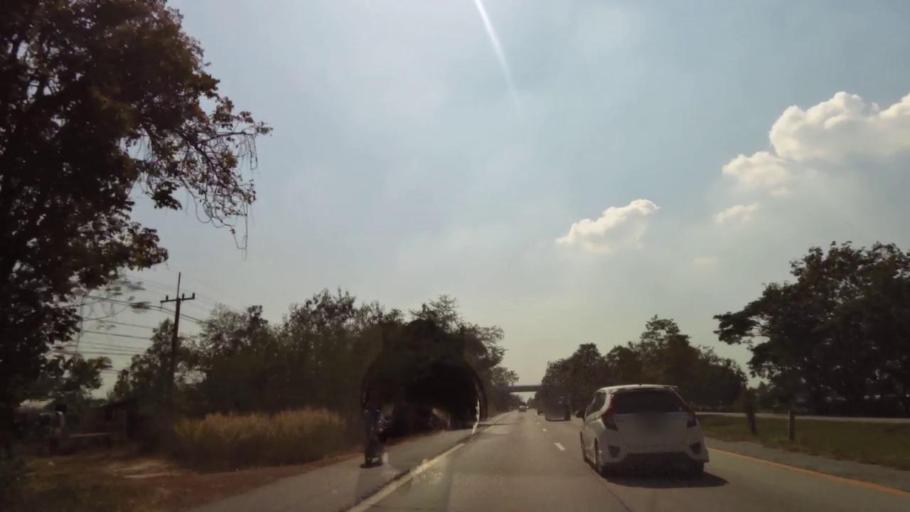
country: TH
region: Phichit
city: Wachira Barami
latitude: 16.5518
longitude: 100.1468
